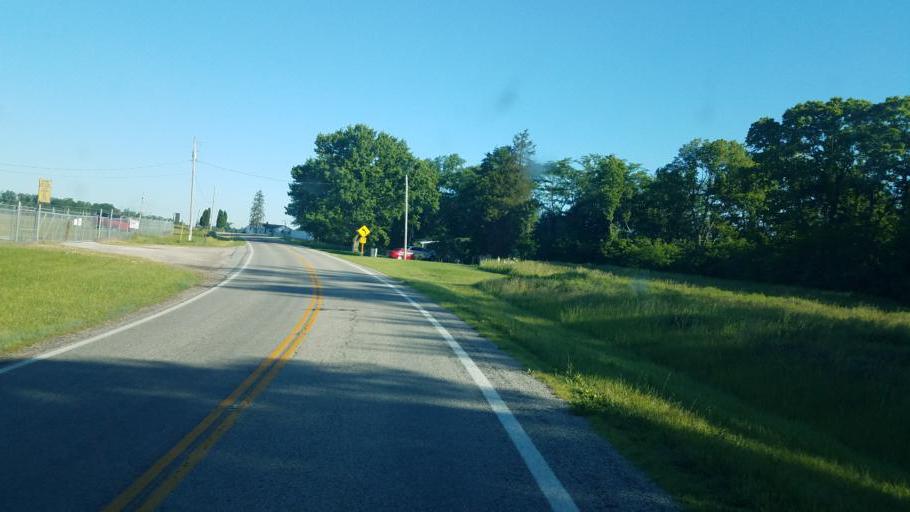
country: US
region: Ohio
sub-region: Morrow County
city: Cardington
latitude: 40.6223
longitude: -82.9629
